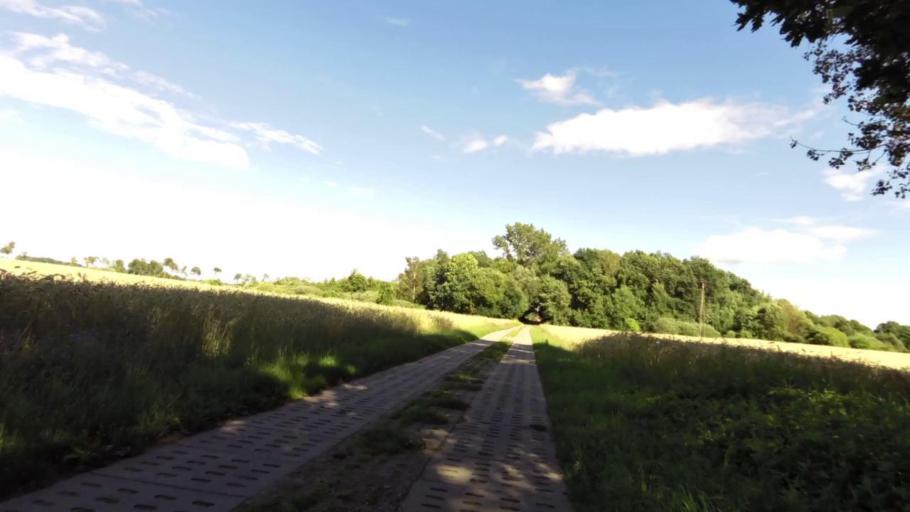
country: PL
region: West Pomeranian Voivodeship
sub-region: Powiat slawienski
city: Slawno
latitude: 54.4618
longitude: 16.7277
